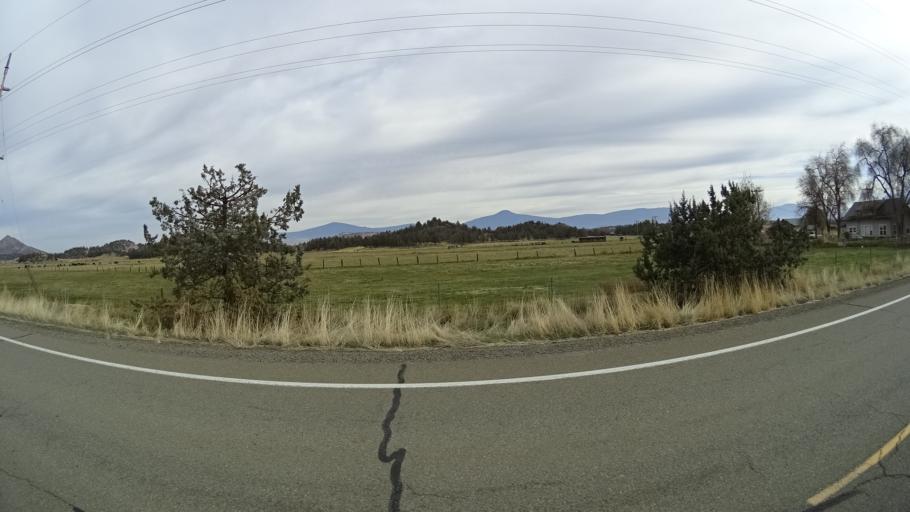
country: US
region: California
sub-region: Siskiyou County
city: Montague
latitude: 41.6739
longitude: -122.5252
